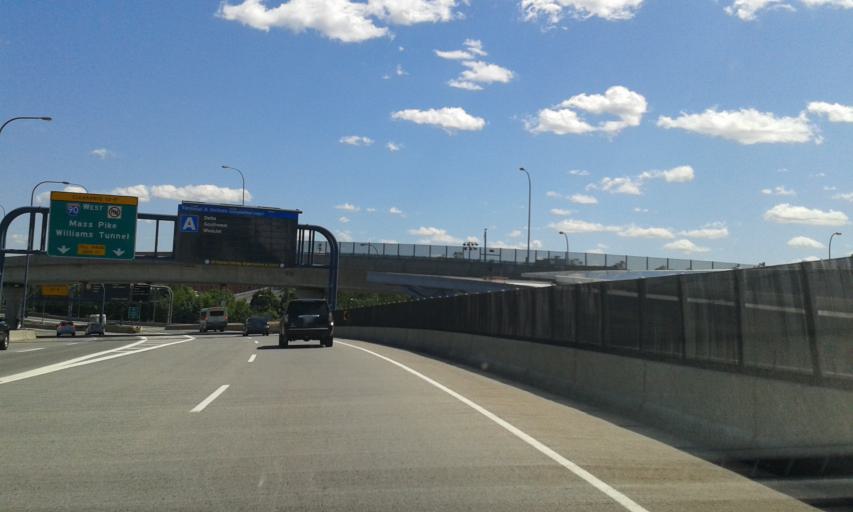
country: US
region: Massachusetts
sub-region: Suffolk County
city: Chelsea
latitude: 42.3747
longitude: -71.0297
